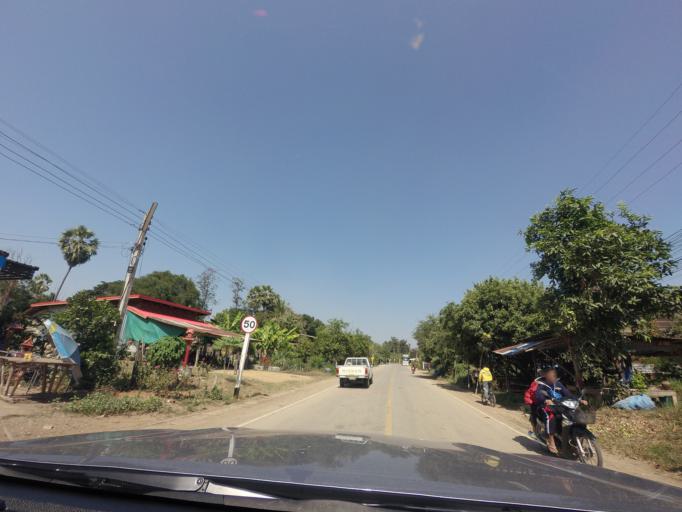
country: TH
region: Sukhothai
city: Si Samrong
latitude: 17.1687
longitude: 99.7699
